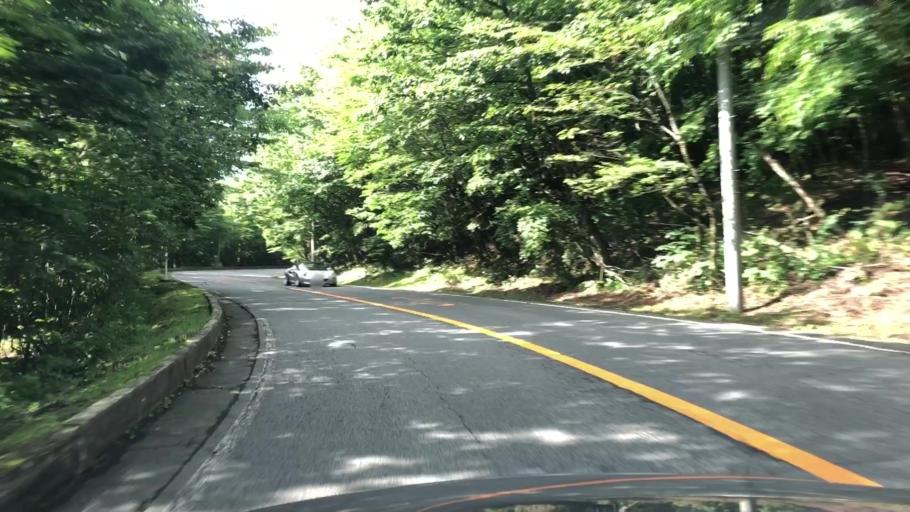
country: JP
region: Shizuoka
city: Gotemba
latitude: 35.3285
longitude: 138.8009
